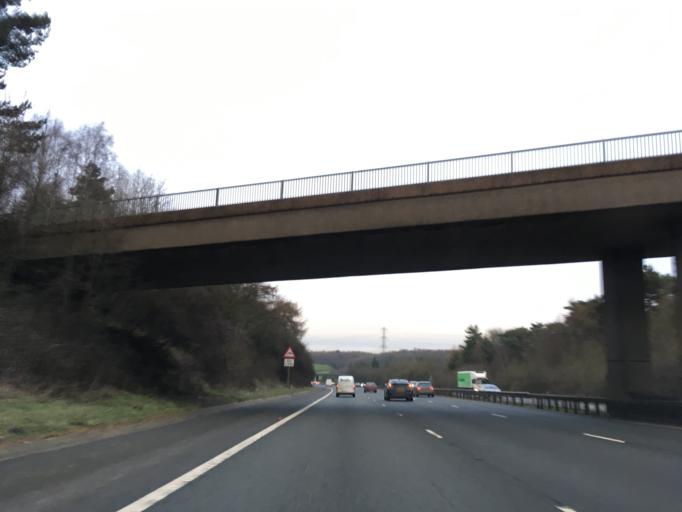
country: GB
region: England
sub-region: South Gloucestershire
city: Tytherington
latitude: 51.6051
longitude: -2.4739
